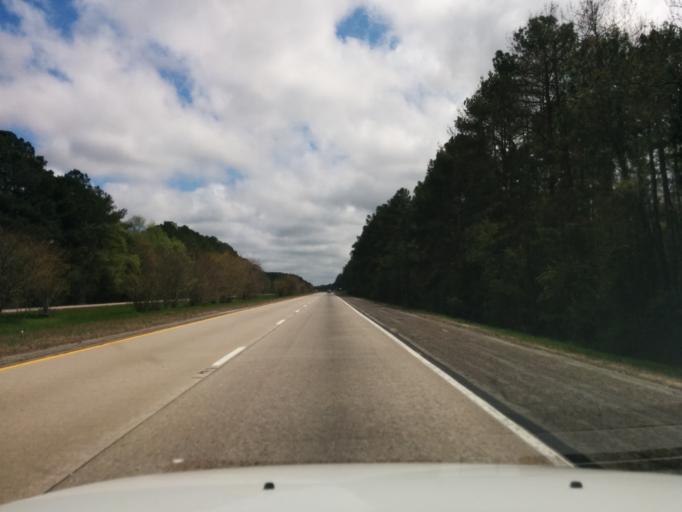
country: US
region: Georgia
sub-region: Chatham County
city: Bloomingdale
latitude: 32.1306
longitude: -81.3962
